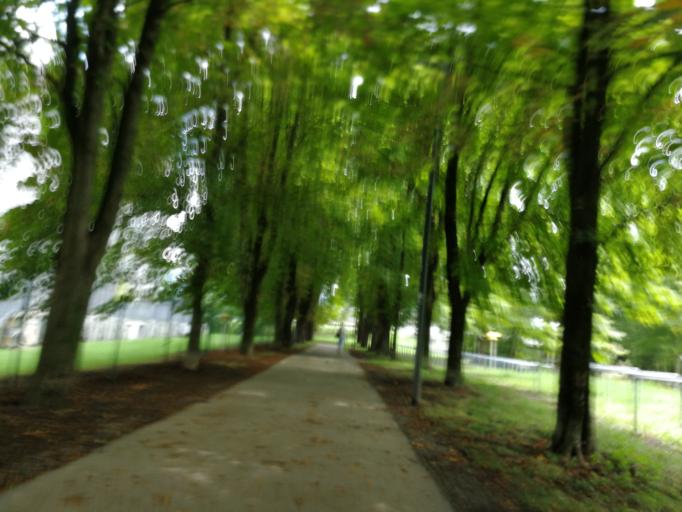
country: DE
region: Bavaria
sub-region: Upper Bavaria
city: Freilassing
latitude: 47.8151
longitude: 12.9988
